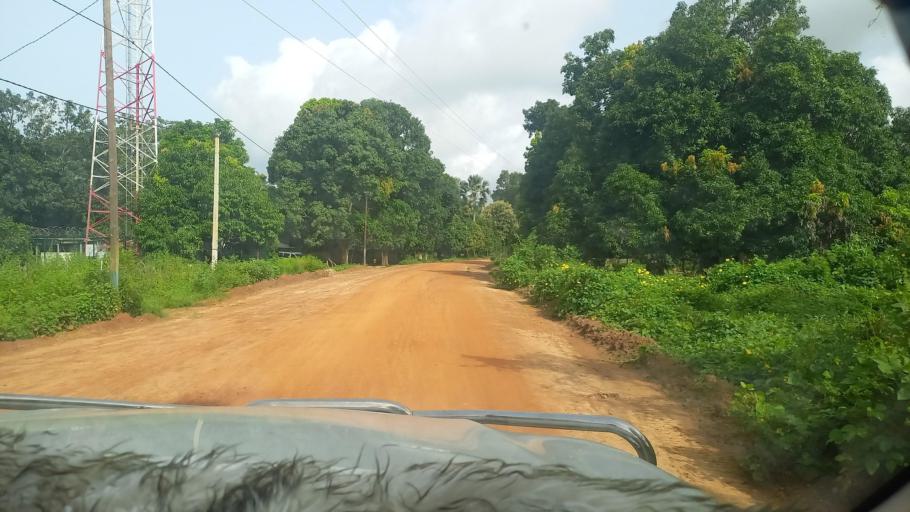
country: SN
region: Ziguinchor
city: Ziguinchor
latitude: 12.6640
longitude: -16.2649
